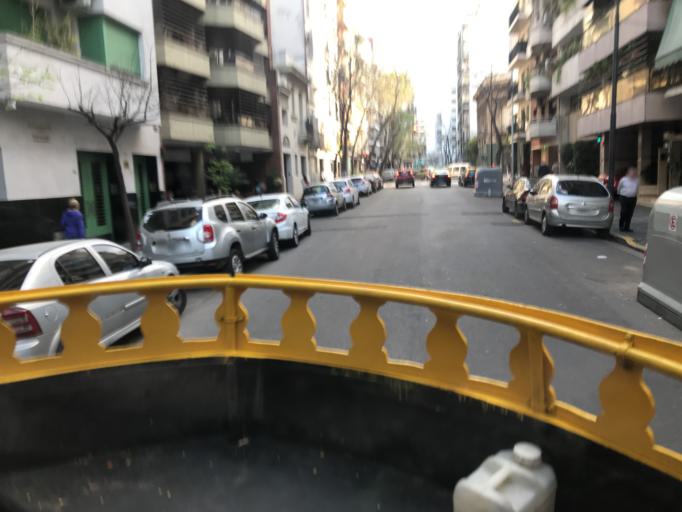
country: AR
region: Buenos Aires F.D.
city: Retiro
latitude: -34.5920
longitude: -58.4075
